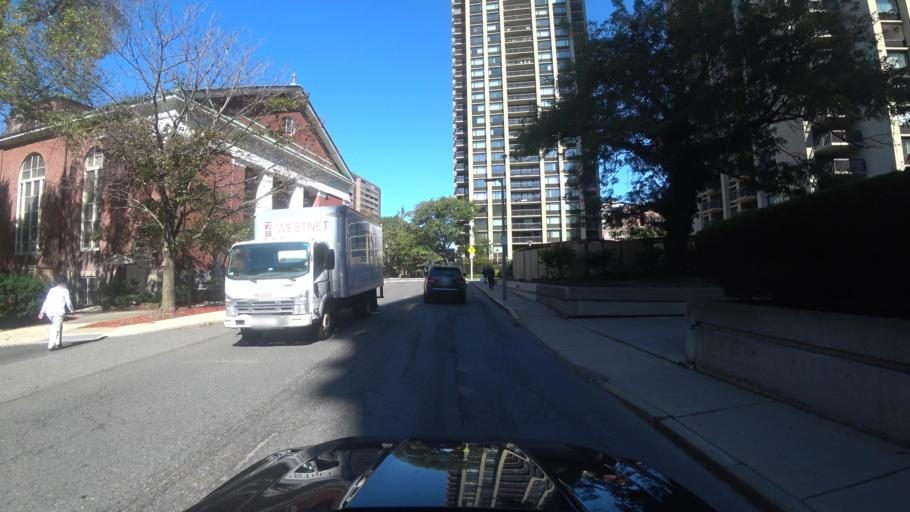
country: US
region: Massachusetts
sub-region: Suffolk County
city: Boston
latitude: 42.3627
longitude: -71.0650
